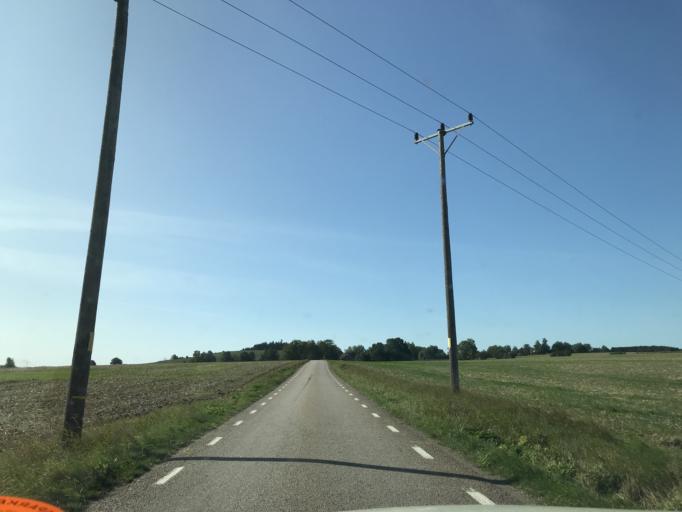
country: SE
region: Skane
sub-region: Landskrona
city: Asmundtorp
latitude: 55.9119
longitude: 12.9531
